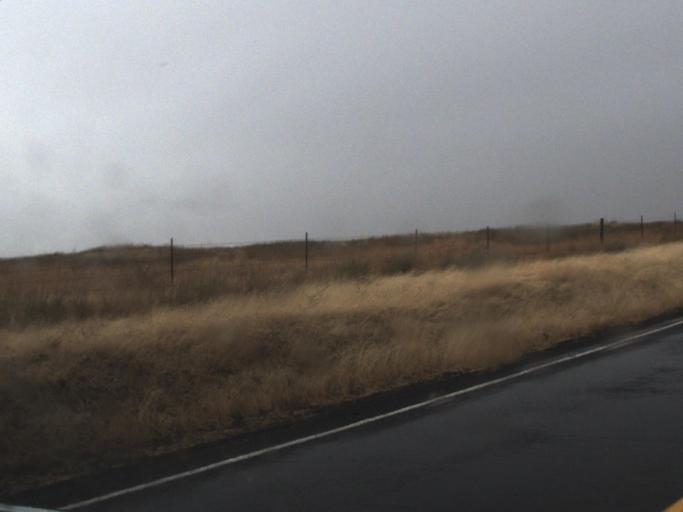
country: US
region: Washington
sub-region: Spokane County
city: Medical Lake
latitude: 47.2216
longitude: -117.9024
